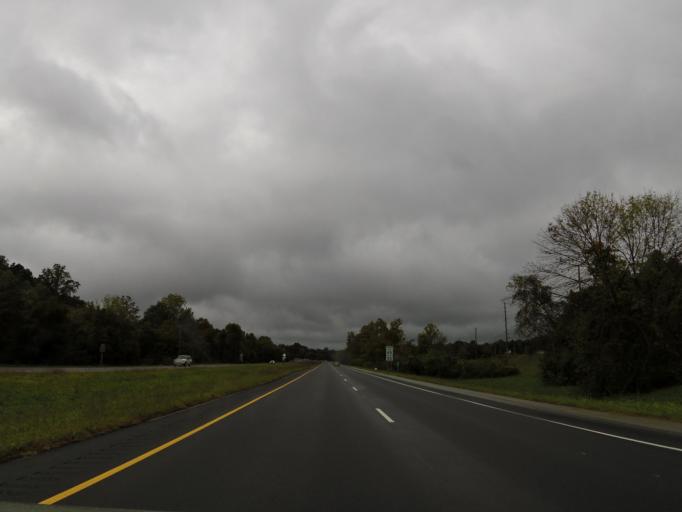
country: US
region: Tennessee
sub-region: Blount County
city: Louisville
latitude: 35.7527
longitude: -84.1245
